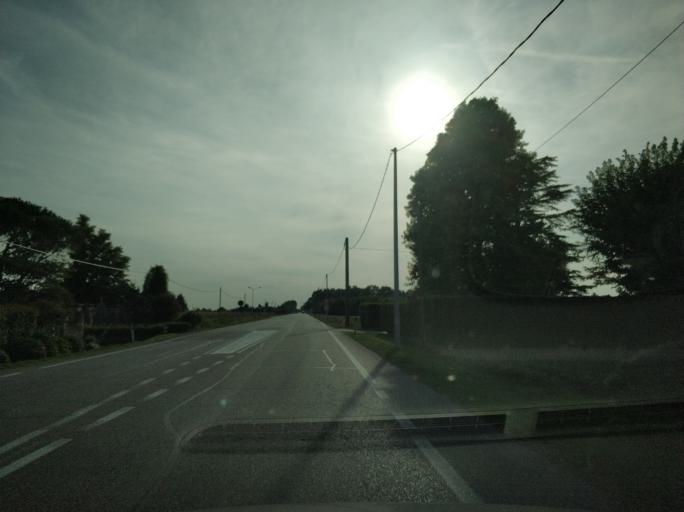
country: IT
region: Veneto
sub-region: Provincia di Padova
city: Correzzola
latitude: 45.2155
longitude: 12.0592
